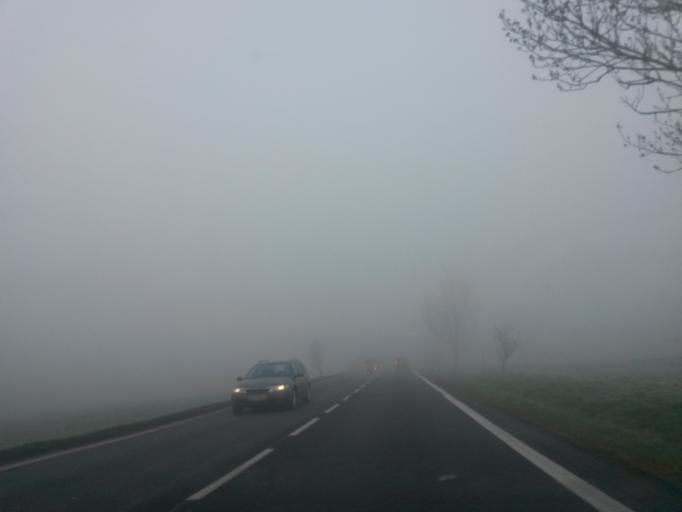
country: CZ
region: Central Bohemia
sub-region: Okres Kladno
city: Slany
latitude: 50.2507
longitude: 14.0352
